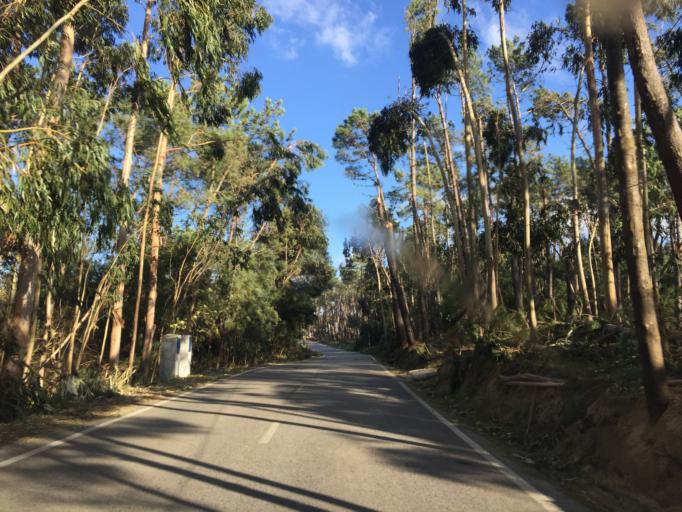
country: PT
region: Coimbra
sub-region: Figueira da Foz
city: Buarcos
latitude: 40.2154
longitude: -8.8690
